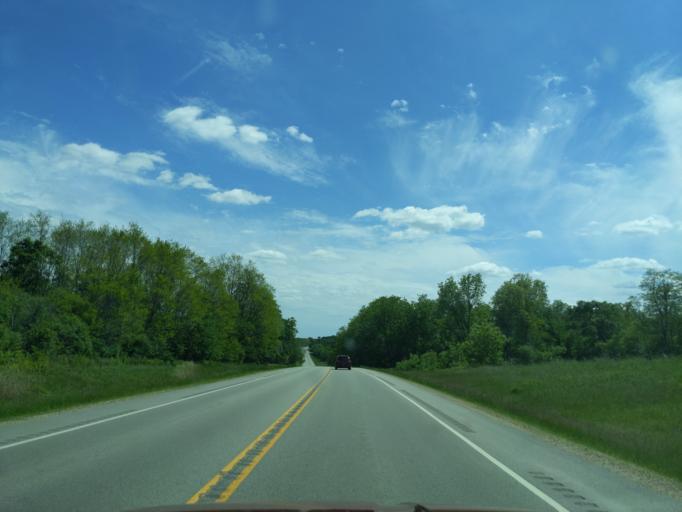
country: US
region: Wisconsin
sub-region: Columbia County
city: Poynette
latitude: 43.4382
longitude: -89.3301
